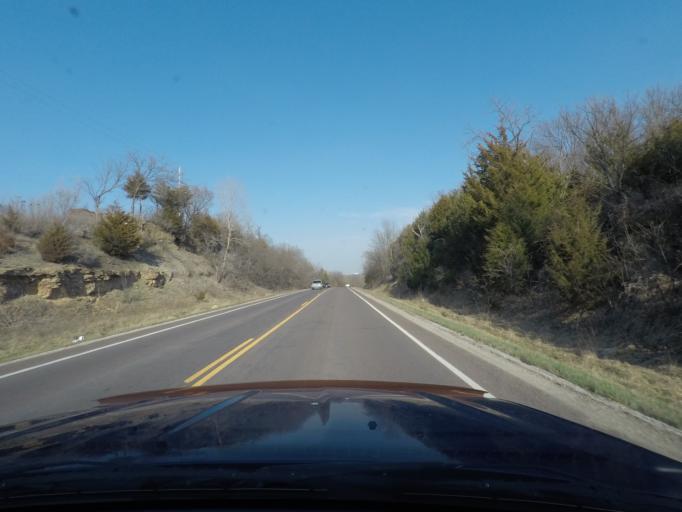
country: US
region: Kansas
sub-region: Douglas County
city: Lawrence
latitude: 39.0008
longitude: -95.3082
